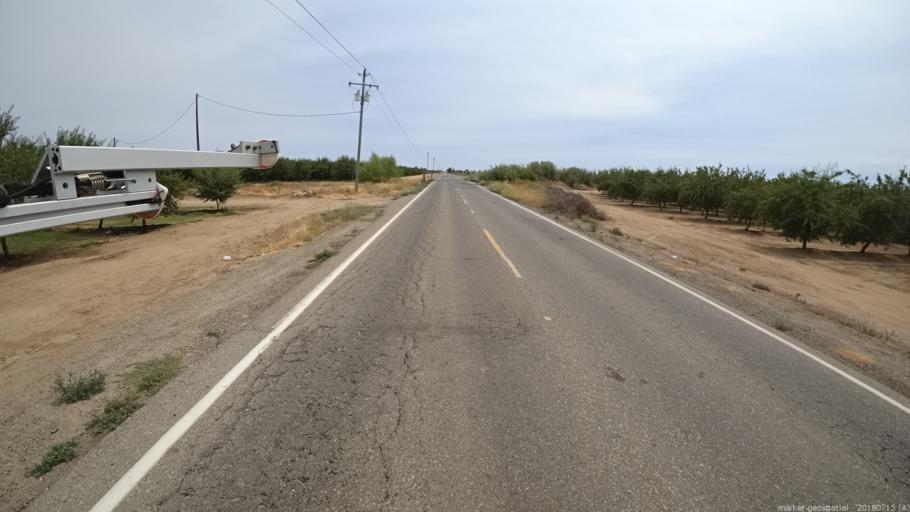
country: US
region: California
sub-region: Madera County
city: Madera Acres
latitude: 37.0204
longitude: -120.1106
